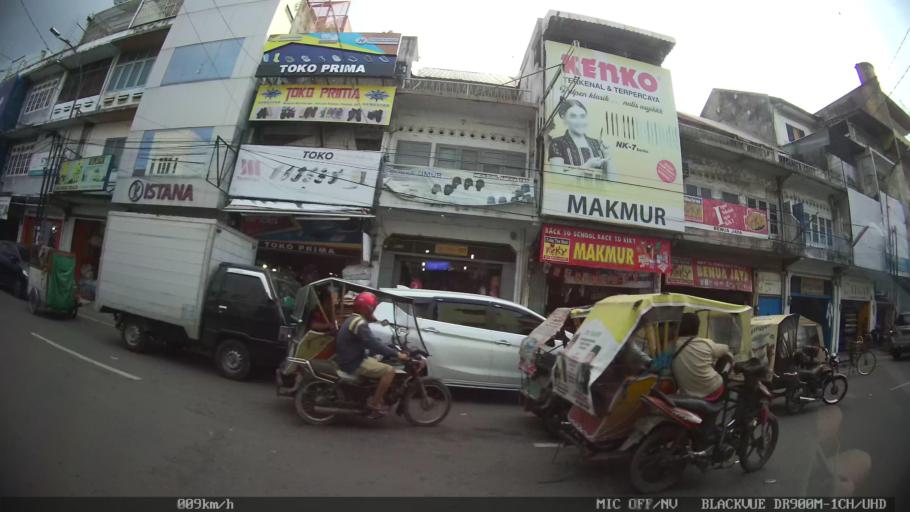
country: ID
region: North Sumatra
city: Medan
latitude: 3.5886
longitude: 98.6842
